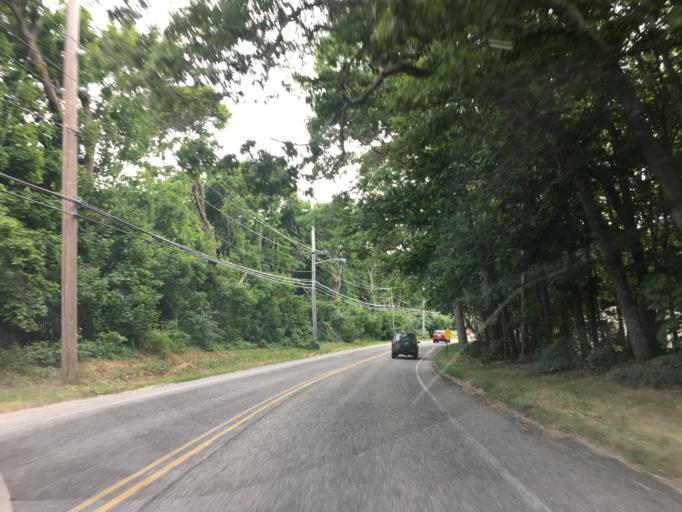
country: US
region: New York
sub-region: Suffolk County
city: Laurel
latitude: 40.9861
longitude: -72.5609
